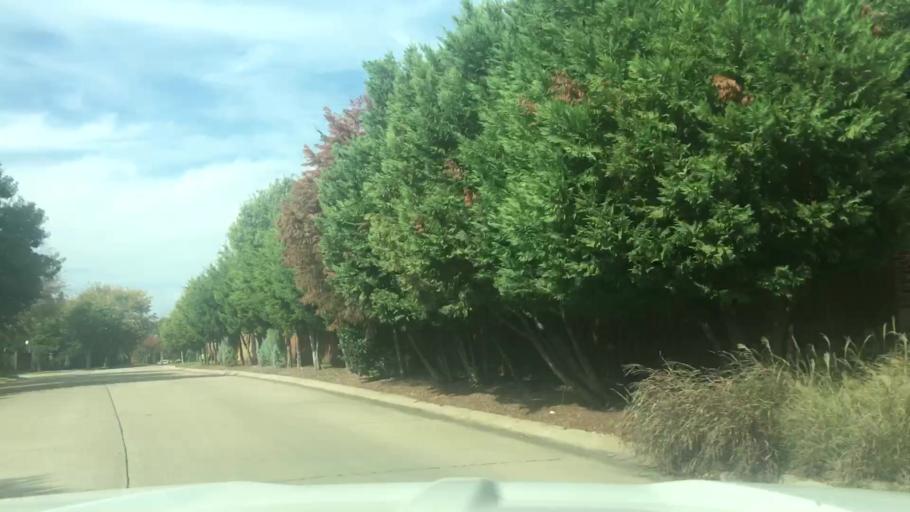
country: US
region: Texas
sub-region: Collin County
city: Prosper
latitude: 33.2303
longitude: -96.7871
